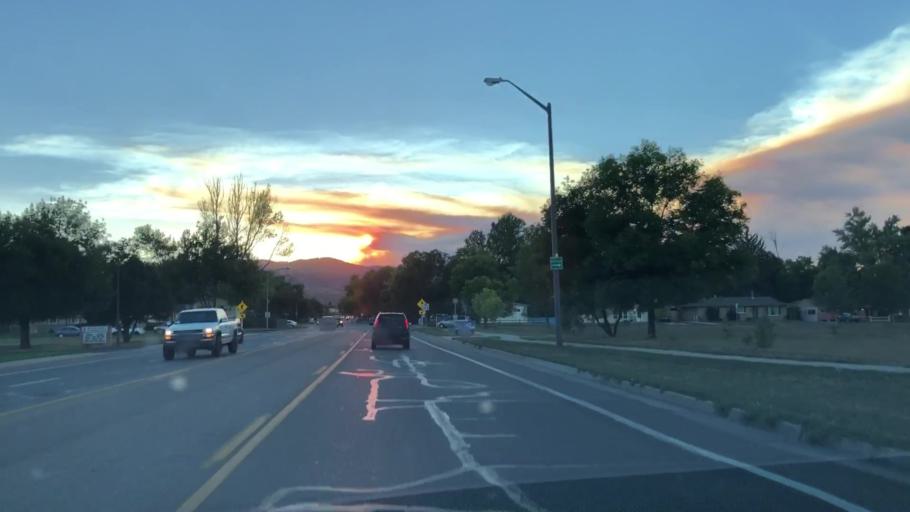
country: US
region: Colorado
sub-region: Larimer County
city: Fort Collins
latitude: 40.5747
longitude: -105.1085
